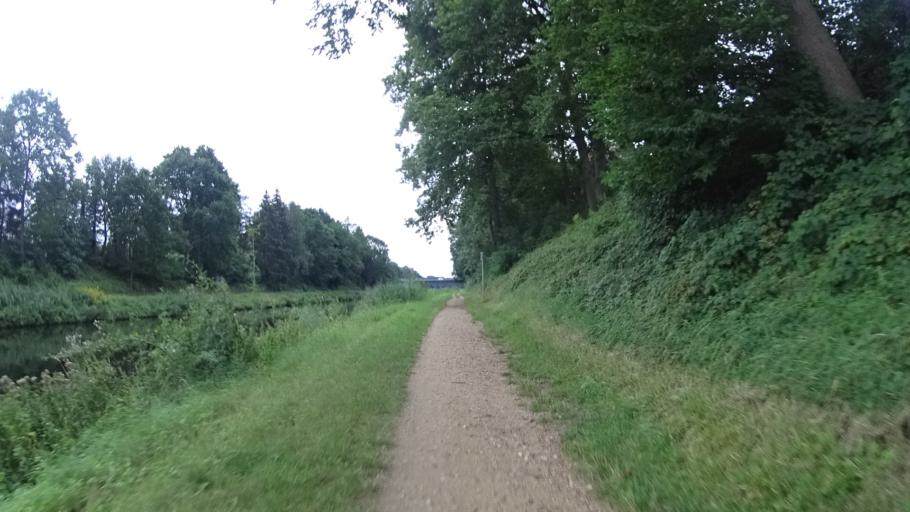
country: DE
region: Schleswig-Holstein
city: Molln
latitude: 53.6244
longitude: 10.6742
